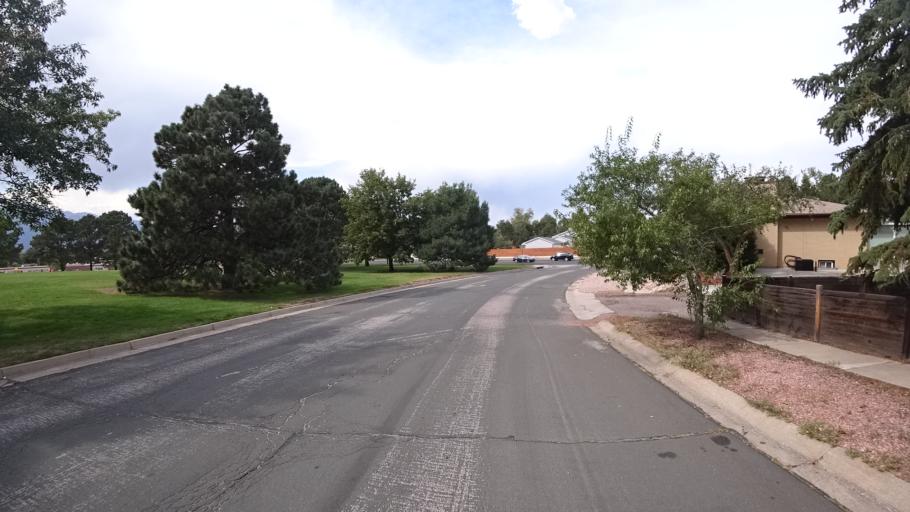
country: US
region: Colorado
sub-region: El Paso County
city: Colorado Springs
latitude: 38.8672
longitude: -104.7808
